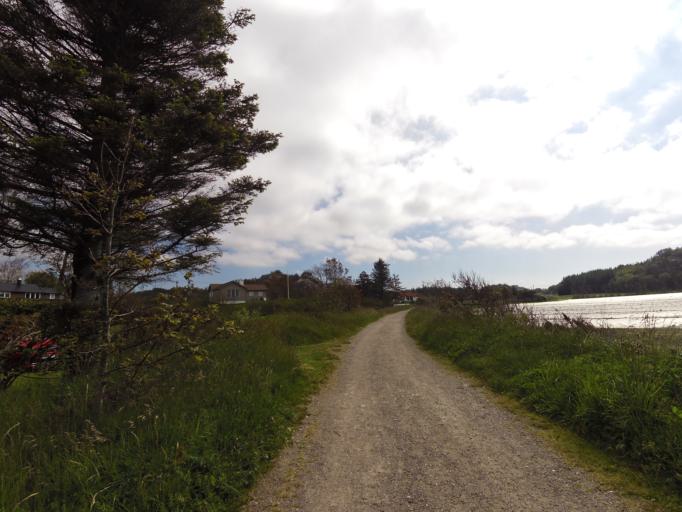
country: NO
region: Rogaland
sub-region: Ha
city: Vigrestad
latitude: 58.5262
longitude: 5.7836
